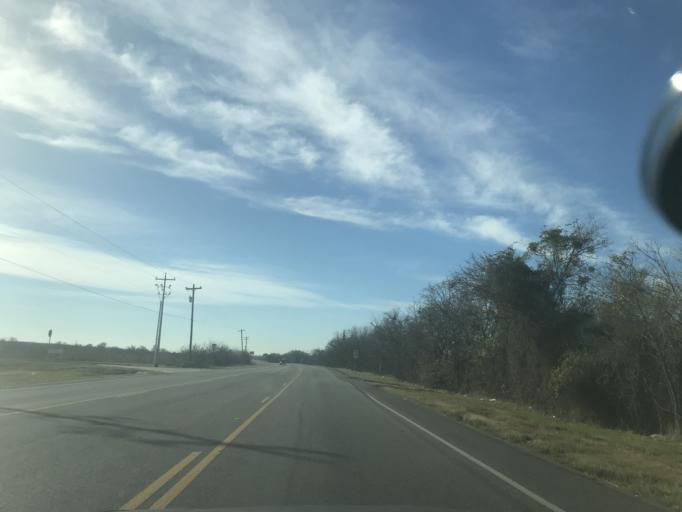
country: US
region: Texas
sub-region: Travis County
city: Manor
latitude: 30.3313
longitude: -97.5601
